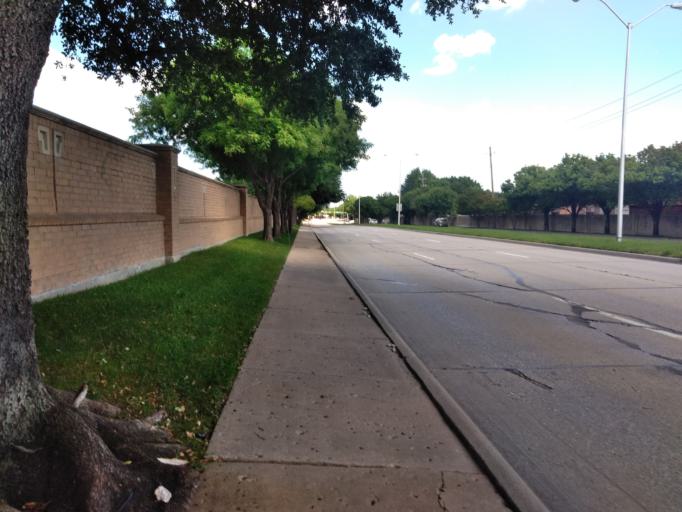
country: US
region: Texas
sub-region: Dallas County
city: Addison
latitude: 32.9993
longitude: -96.8213
